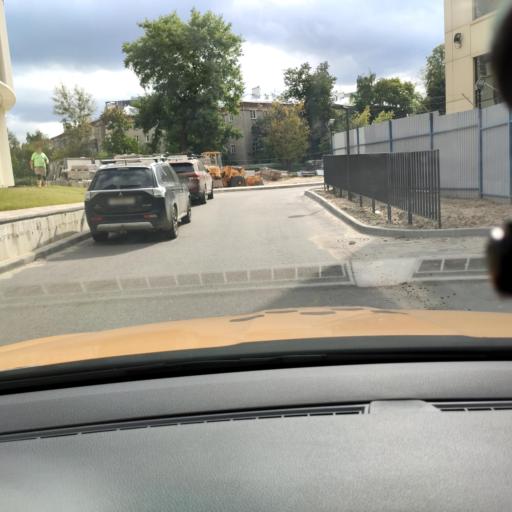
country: RU
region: Moscow
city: Sokol'niki
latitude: 55.8115
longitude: 37.6469
